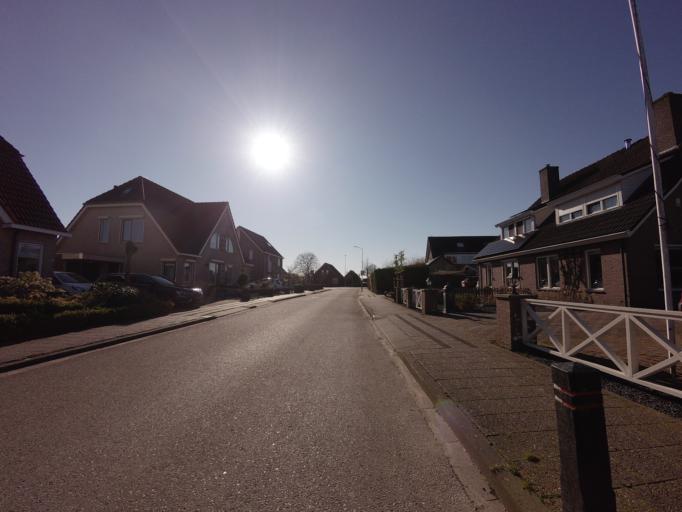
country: NL
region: Utrecht
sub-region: Gemeente Utrechtse Heuvelrug
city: Leersum
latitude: 51.9575
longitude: 5.4209
